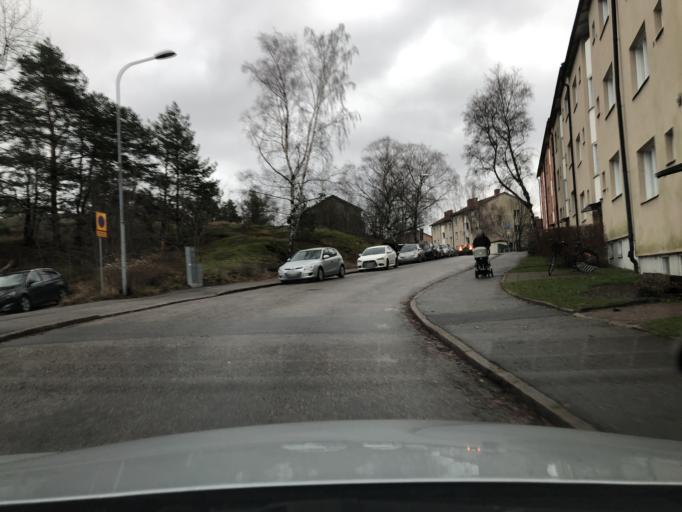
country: SE
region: Stockholm
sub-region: Stockholms Kommun
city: Arsta
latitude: 59.2991
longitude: 18.0421
